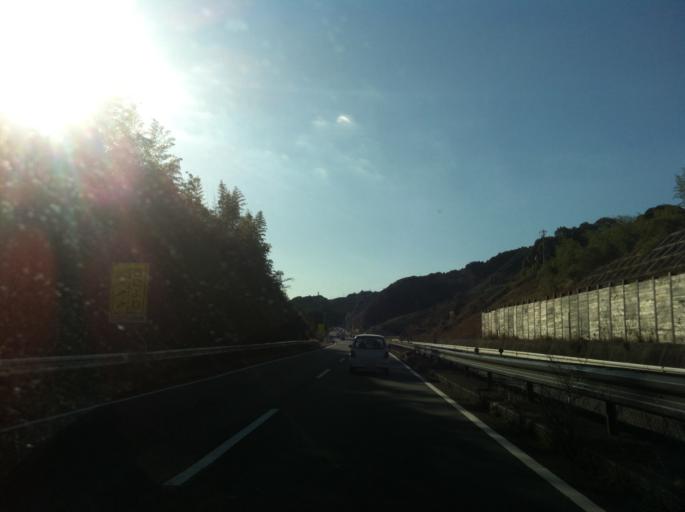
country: JP
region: Shizuoka
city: Kanaya
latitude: 34.8333
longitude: 138.1176
